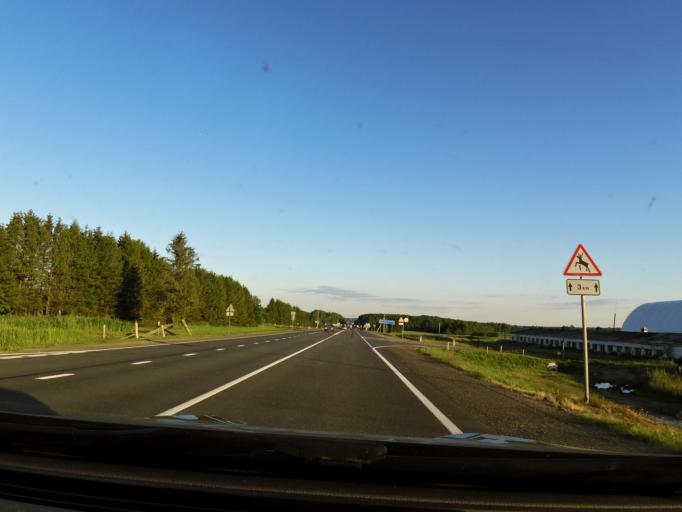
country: RU
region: Vologda
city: Gryazovets
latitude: 58.7699
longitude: 40.2769
